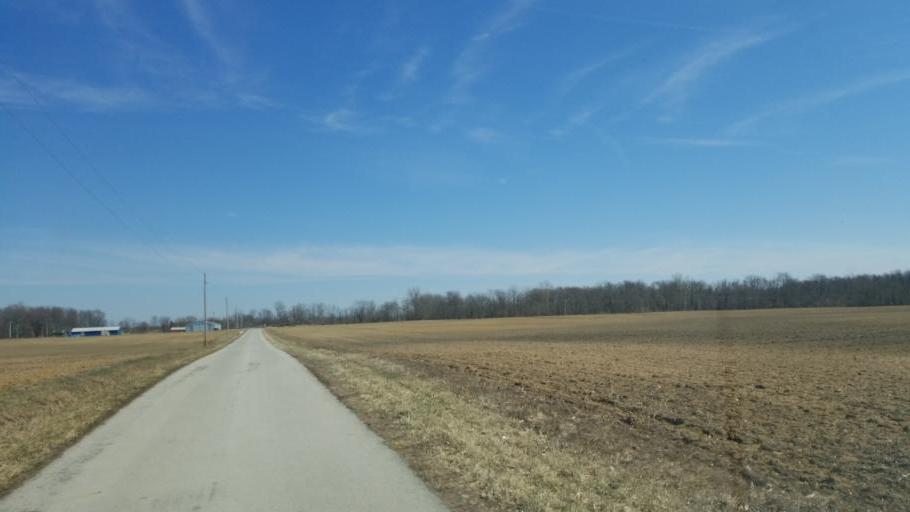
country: US
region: Ohio
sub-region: Crawford County
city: Bucyrus
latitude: 40.6651
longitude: -82.9526
